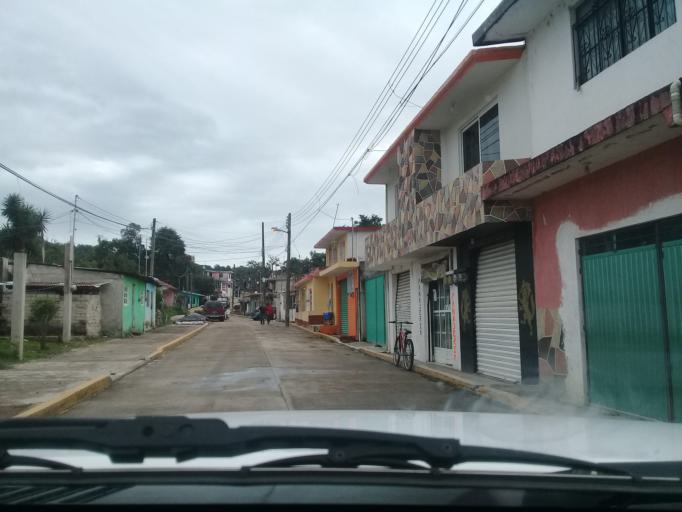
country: MX
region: Veracruz
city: Rafael Lucio
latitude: 19.5931
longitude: -96.9876
